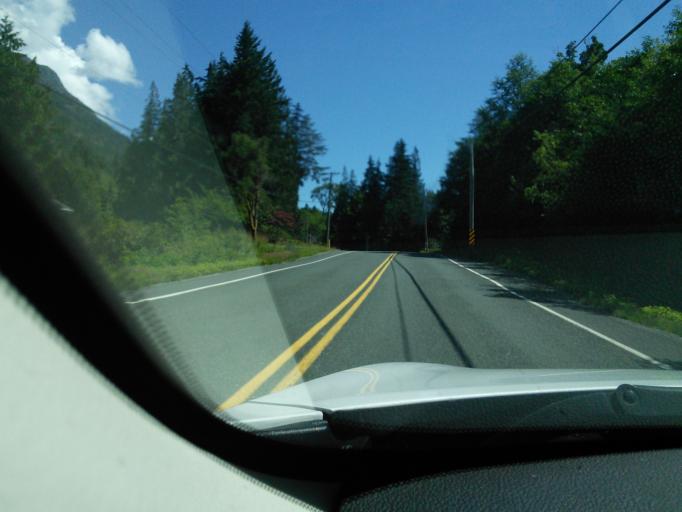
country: CA
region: British Columbia
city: Campbell River
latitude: 50.3525
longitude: -125.9079
